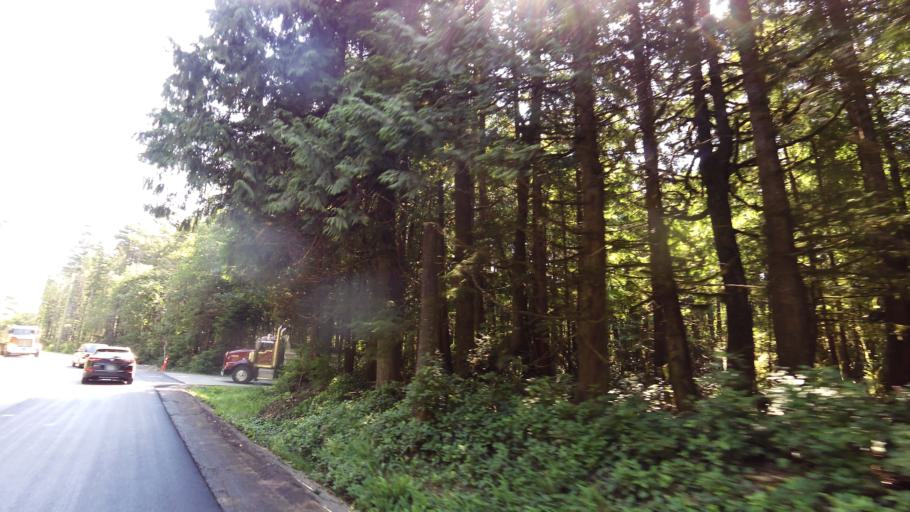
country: CA
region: British Columbia
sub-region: Regional District of Alberni-Clayoquot
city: Ucluelet
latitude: 49.0138
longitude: -125.6519
